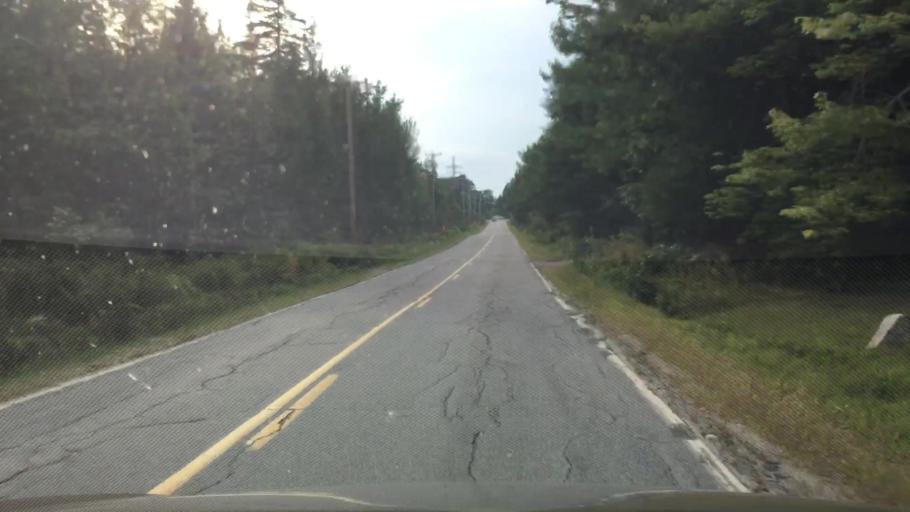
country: US
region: Maine
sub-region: Hancock County
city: Penobscot
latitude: 44.4736
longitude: -68.7741
